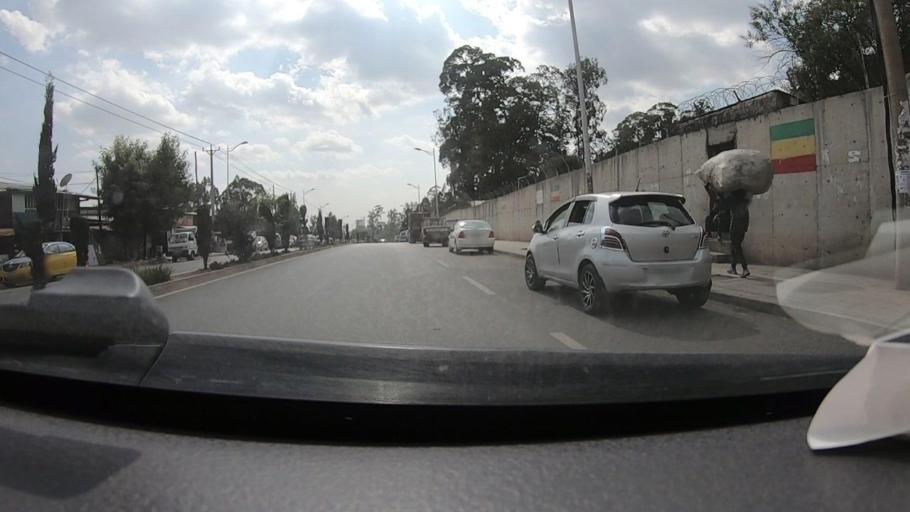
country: ET
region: Adis Abeba
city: Addis Ababa
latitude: 9.0551
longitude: 38.7736
